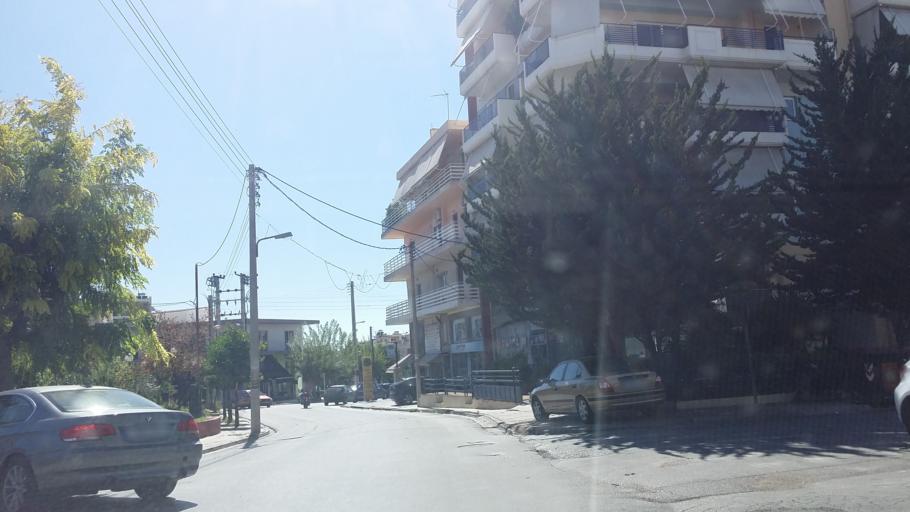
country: GR
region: Attica
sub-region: Nomarchia Athinas
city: Peristeri
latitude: 38.0182
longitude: 23.7006
